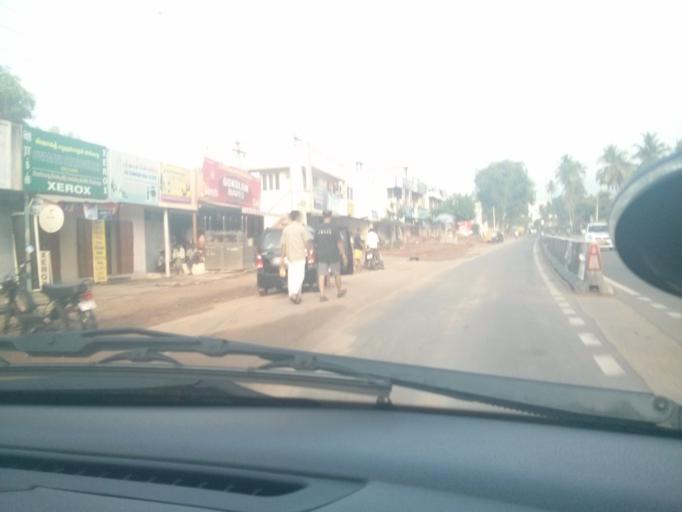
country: IN
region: Tamil Nadu
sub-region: Coimbatore
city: Perur
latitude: 11.0283
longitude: 76.9018
